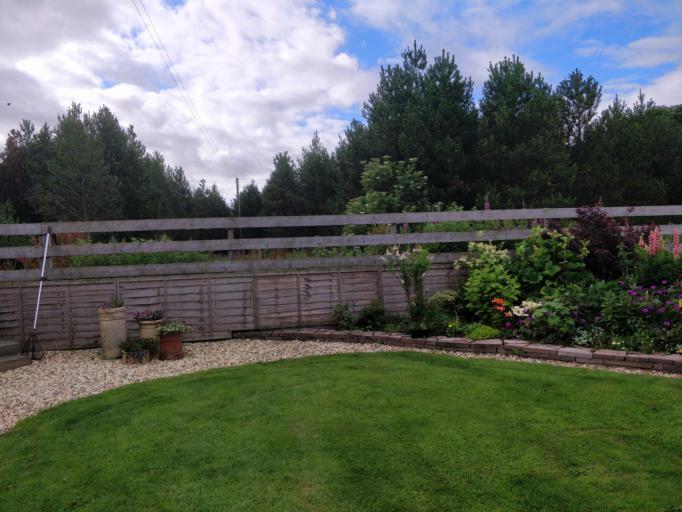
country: GB
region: Scotland
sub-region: Highland
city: Thurso
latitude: 58.4676
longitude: -3.4277
